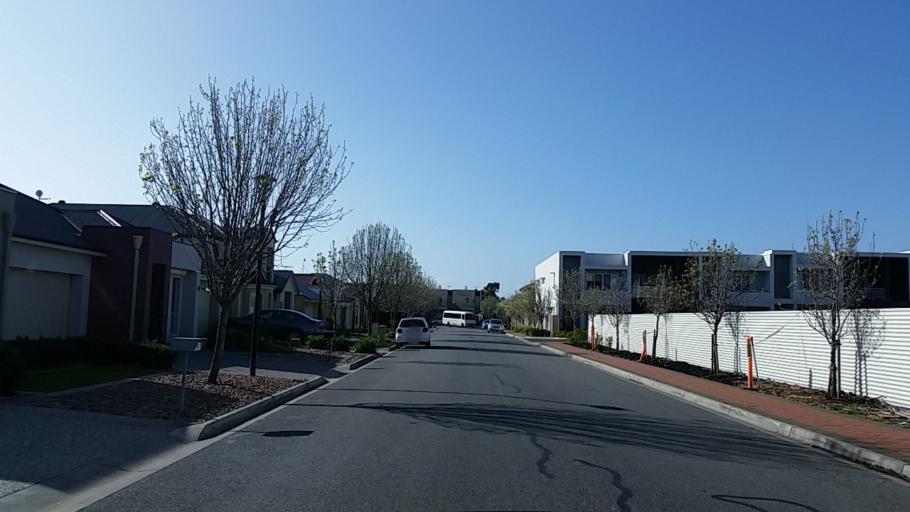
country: AU
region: South Australia
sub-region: Charles Sturt
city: Findon
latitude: -34.9037
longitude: 138.5284
